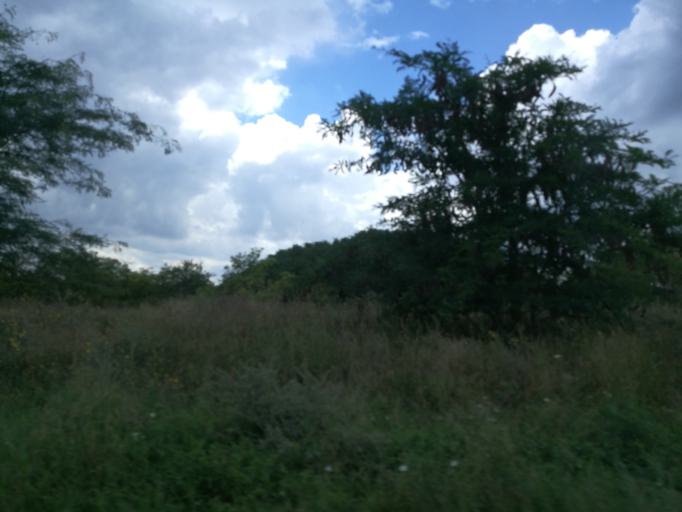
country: RO
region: Constanta
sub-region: Comuna Sacele
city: Sacele
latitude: 44.4462
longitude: 28.7334
